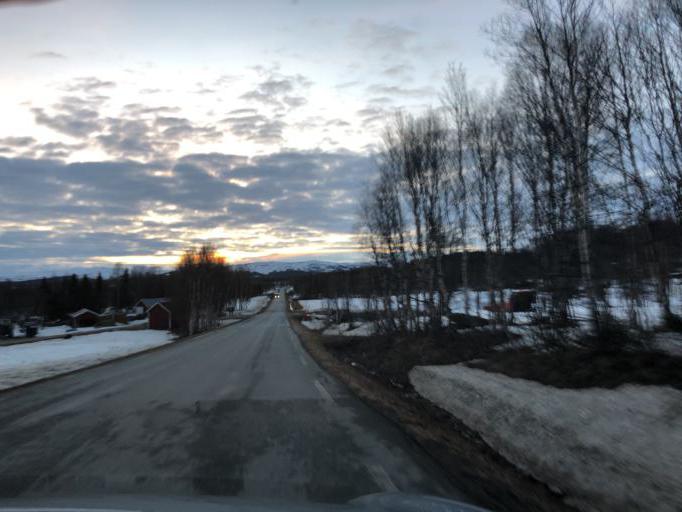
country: NO
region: Sor-Trondelag
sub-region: Tydal
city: Aas
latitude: 62.6820
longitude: 11.7779
